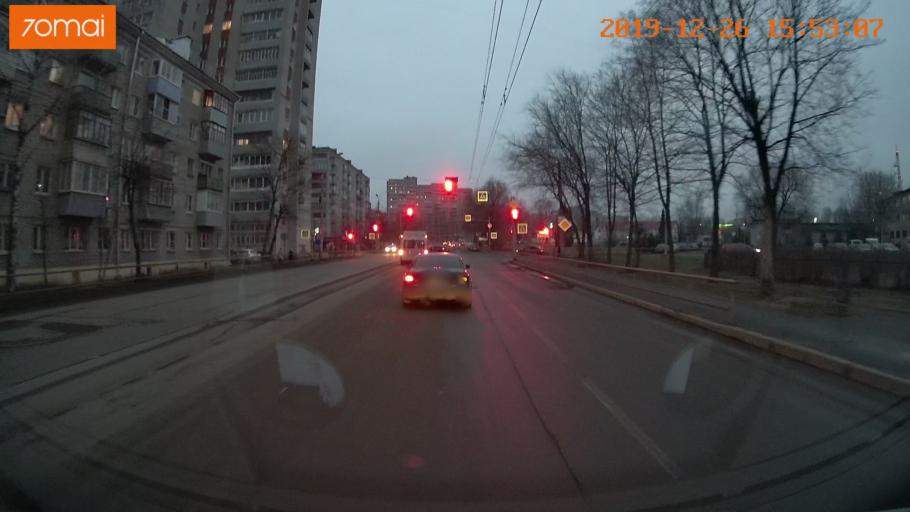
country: RU
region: Jaroslavl
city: Rybinsk
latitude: 58.0486
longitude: 38.8230
